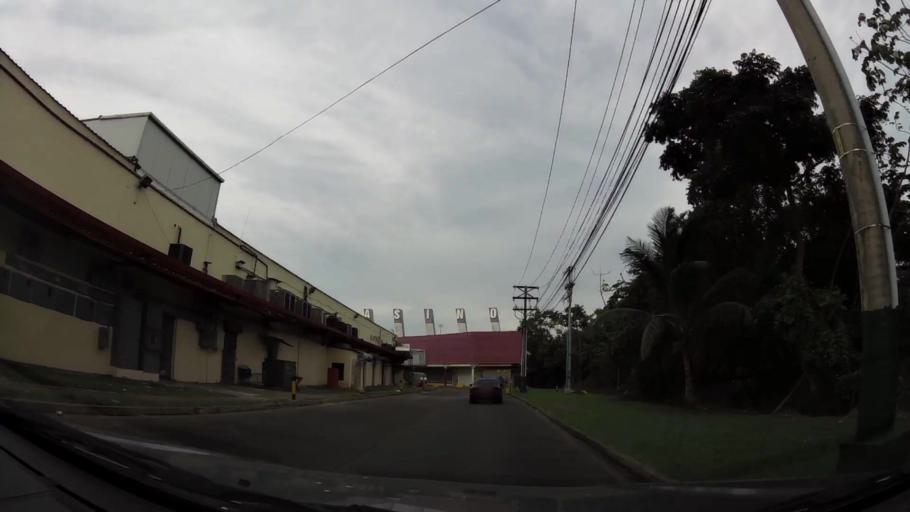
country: PA
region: Panama
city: San Miguelito
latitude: 9.0496
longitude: -79.4477
